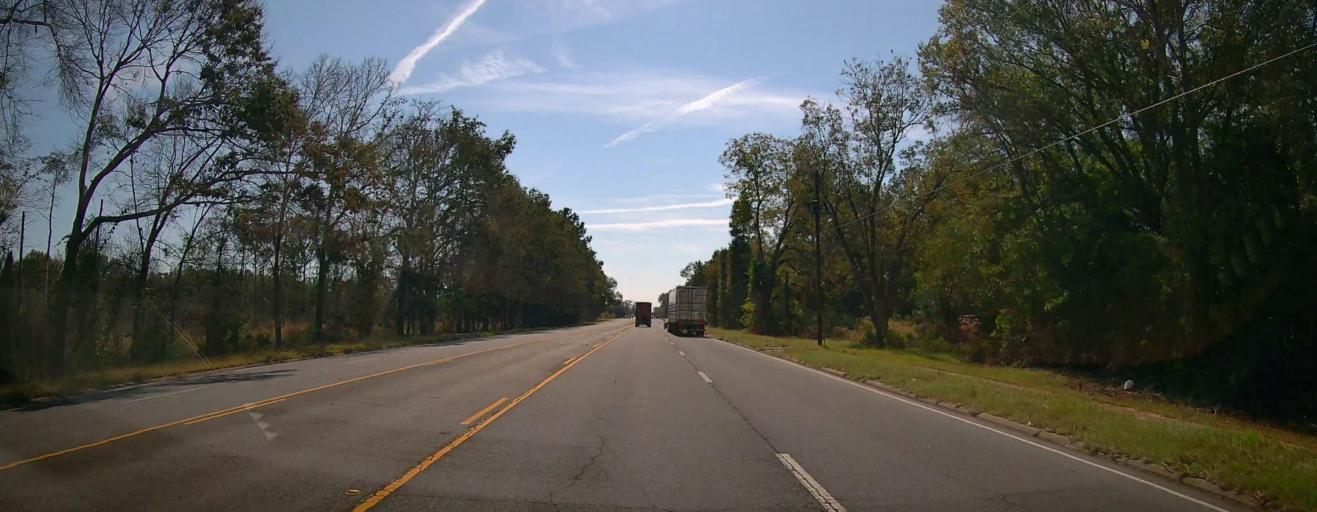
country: US
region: Georgia
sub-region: Lee County
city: Leesburg
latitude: 31.7826
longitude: -83.9652
